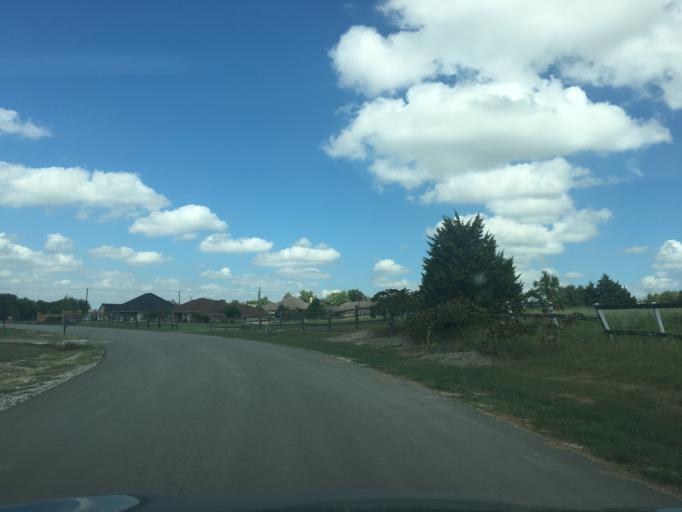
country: US
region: Texas
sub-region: Dallas County
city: Sachse
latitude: 32.9580
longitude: -96.5588
